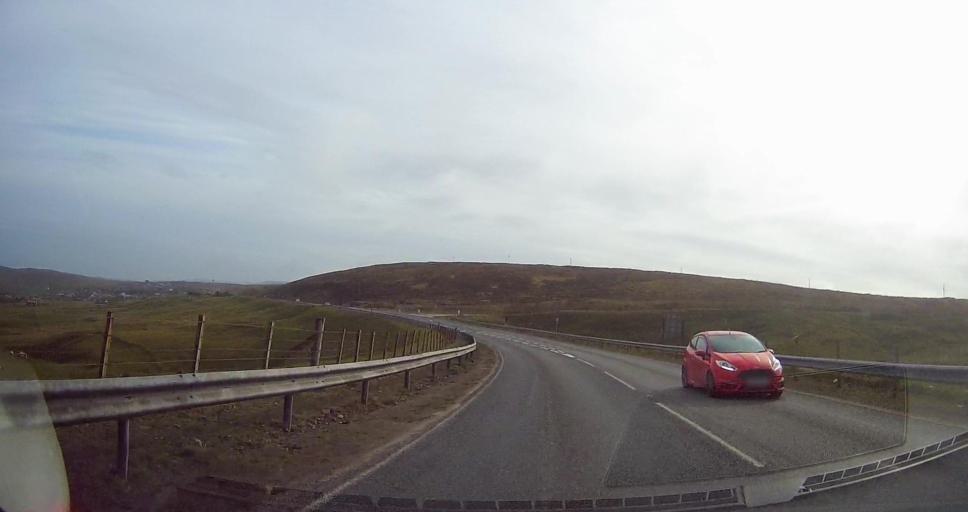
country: GB
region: Scotland
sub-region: Shetland Islands
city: Lerwick
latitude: 60.1388
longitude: -1.2112
